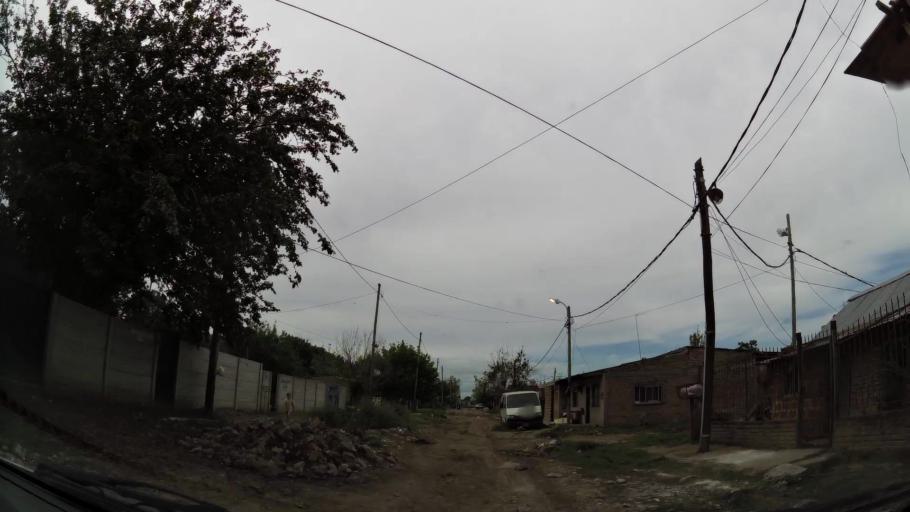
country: AR
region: Buenos Aires
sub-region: Partido de Quilmes
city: Quilmes
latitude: -34.7549
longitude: -58.2551
